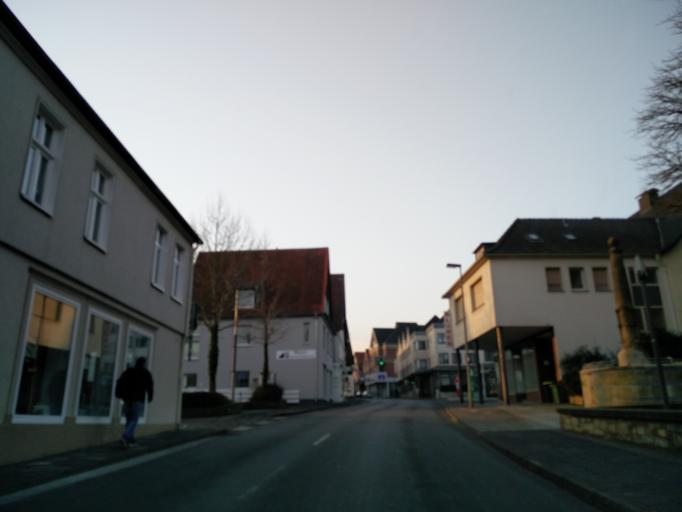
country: DE
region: North Rhine-Westphalia
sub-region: Regierungsbezirk Detmold
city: Buren
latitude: 51.5531
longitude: 8.5600
